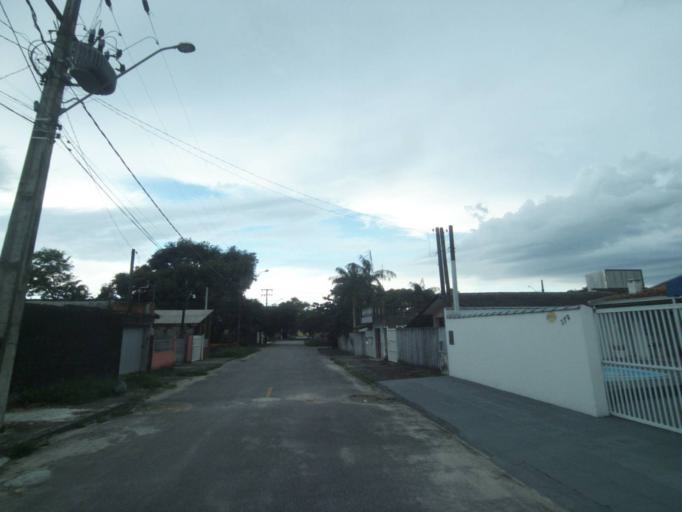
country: BR
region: Parana
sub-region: Guaratuba
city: Guaratuba
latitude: -25.8179
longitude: -48.5413
